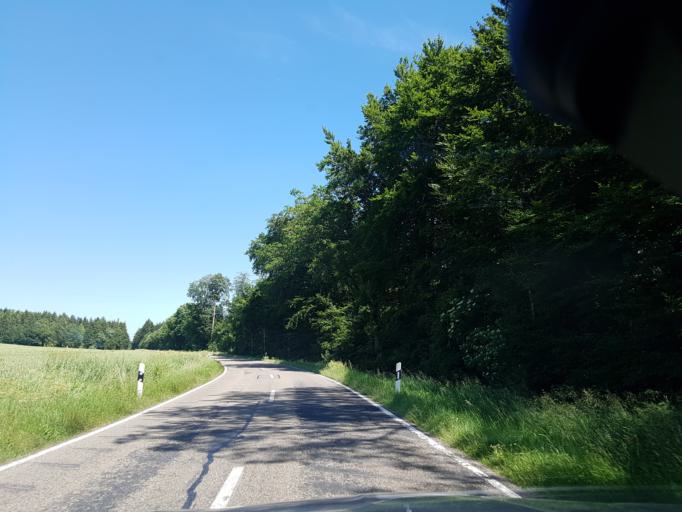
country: DE
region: Baden-Wuerttemberg
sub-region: Tuebingen Region
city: Blaubeuren
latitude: 48.4163
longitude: 9.8316
